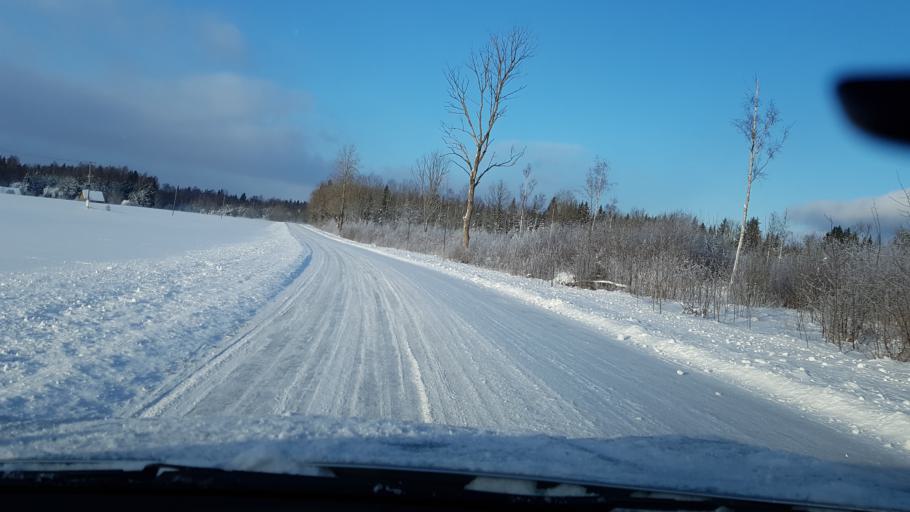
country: EE
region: Harju
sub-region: Nissi vald
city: Turba
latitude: 59.1094
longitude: 24.2279
